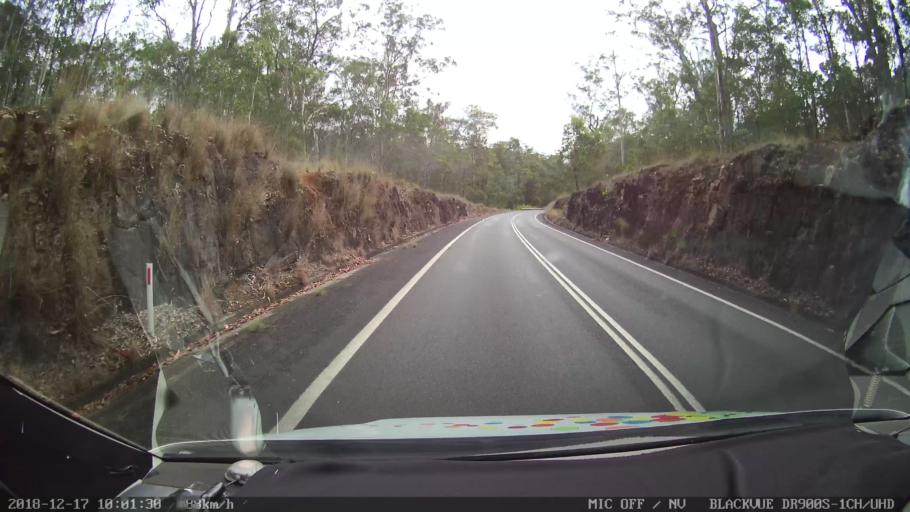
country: AU
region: New South Wales
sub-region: Tenterfield Municipality
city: Carrolls Creek
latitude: -28.9039
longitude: 152.4386
